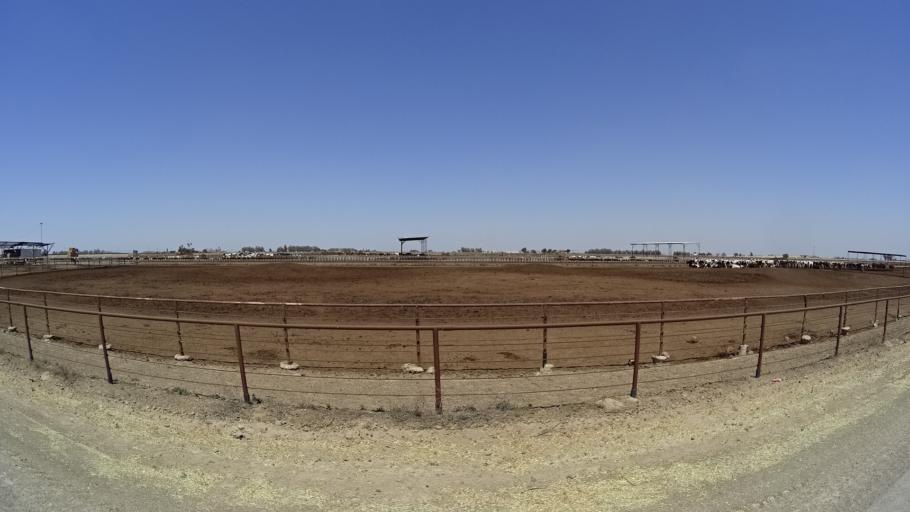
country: US
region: California
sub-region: Kings County
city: Home Garden
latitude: 36.1968
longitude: -119.6318
